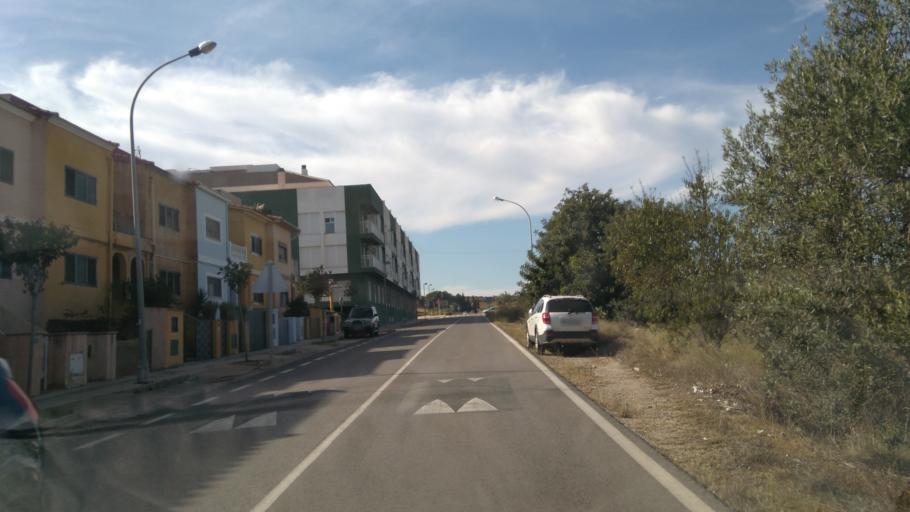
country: ES
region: Valencia
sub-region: Provincia de Valencia
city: Montroy
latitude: 39.3430
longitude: -0.6155
